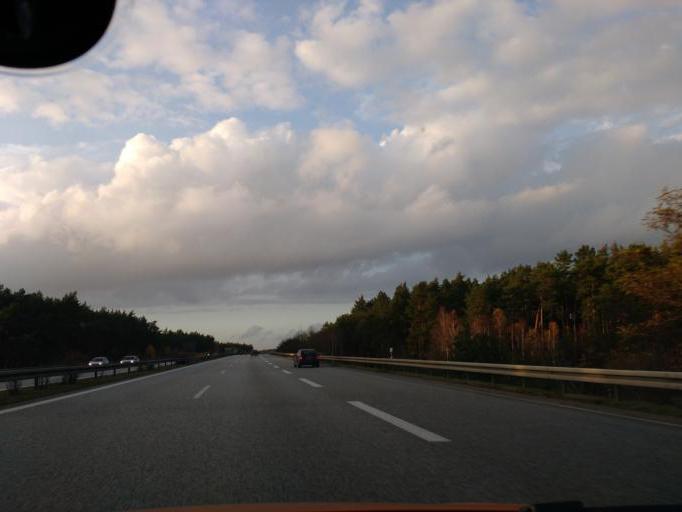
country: DE
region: Mecklenburg-Vorpommern
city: Neustadt-Glewe
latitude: 53.3813
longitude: 11.6199
